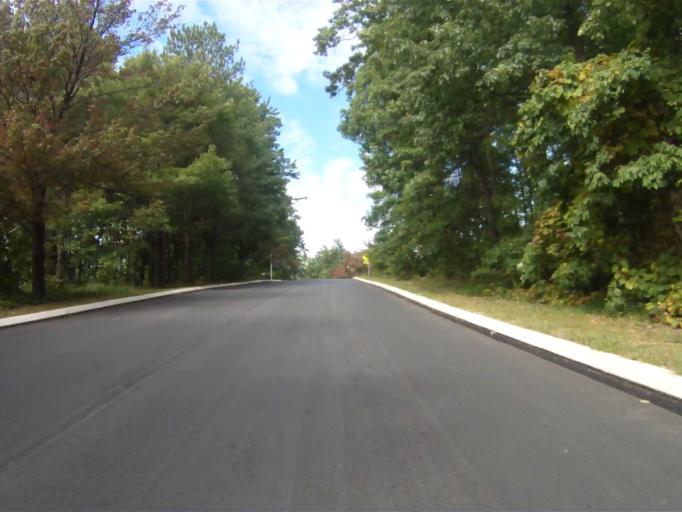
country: US
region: Pennsylvania
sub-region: Centre County
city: Park Forest Village
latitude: 40.8061
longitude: -77.9213
